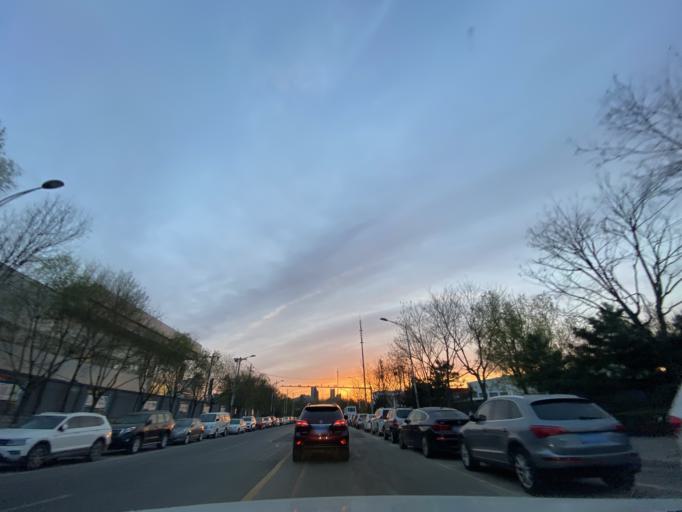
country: CN
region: Beijing
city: Qinghe
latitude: 40.0162
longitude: 116.3544
